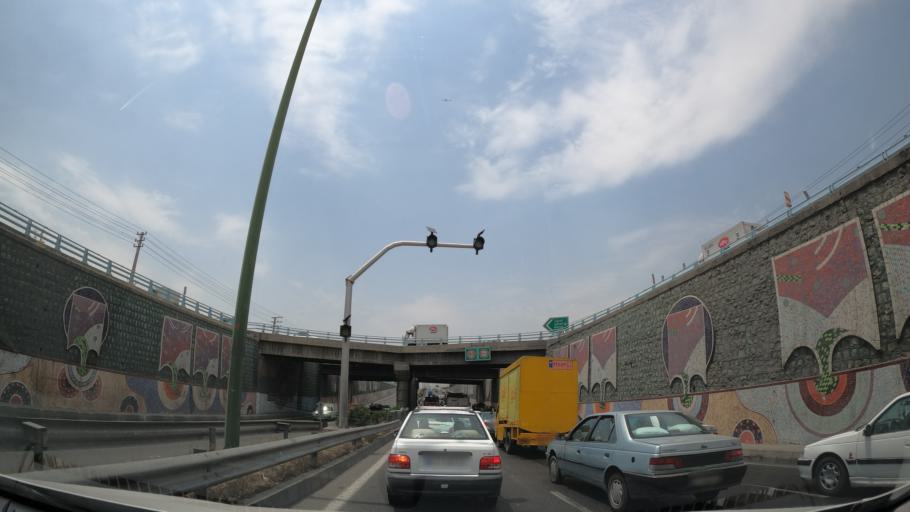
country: IR
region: Tehran
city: Shahr-e Qods
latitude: 35.6918
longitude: 51.2125
